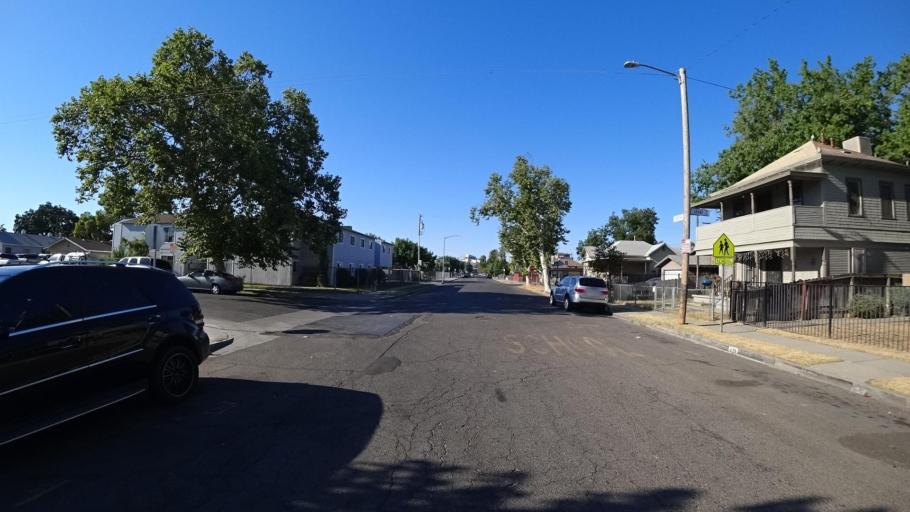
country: US
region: California
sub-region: Fresno County
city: Fresno
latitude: 36.7493
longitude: -119.7838
